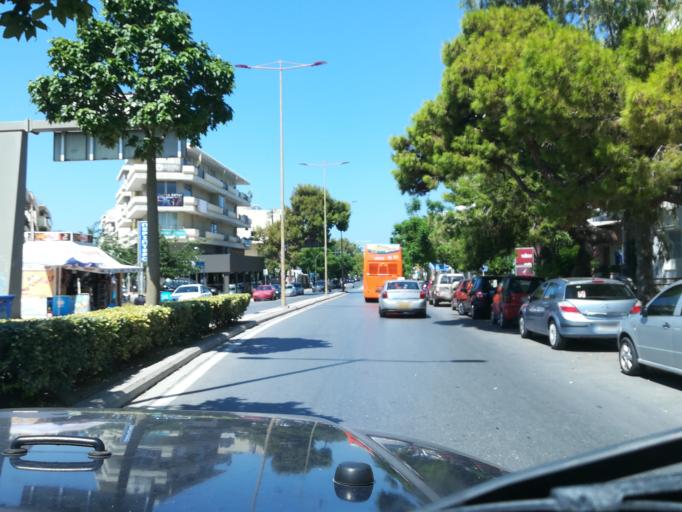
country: GR
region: Crete
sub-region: Nomos Irakleiou
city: Irakleion
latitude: 35.3287
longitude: 25.1380
